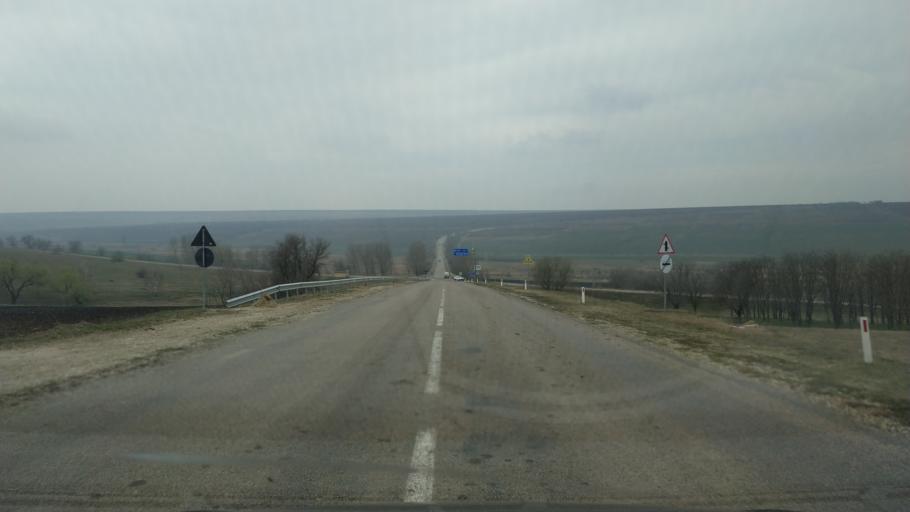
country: MD
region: Cahul
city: Cahul
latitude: 45.9599
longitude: 28.4124
